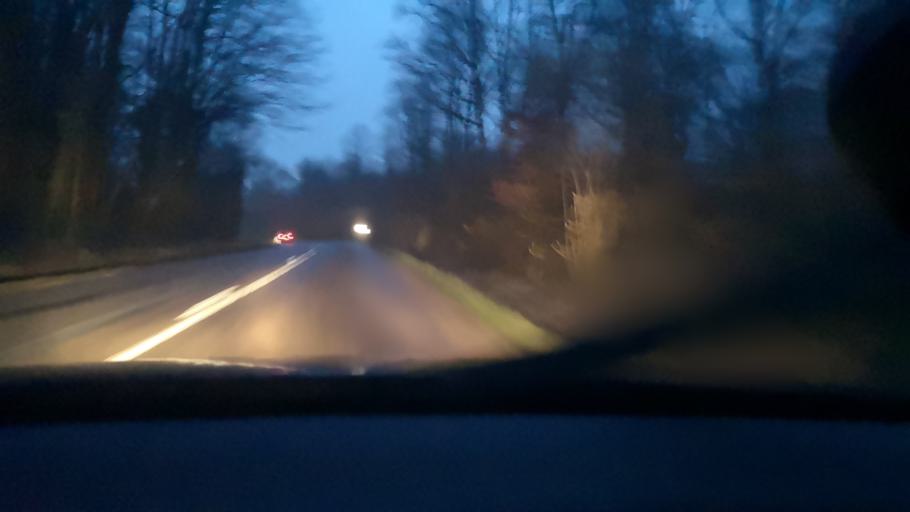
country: FR
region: Bourgogne
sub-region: Departement de Saone-et-Loire
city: Virey-le-Grand
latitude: 46.8787
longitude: 4.8518
